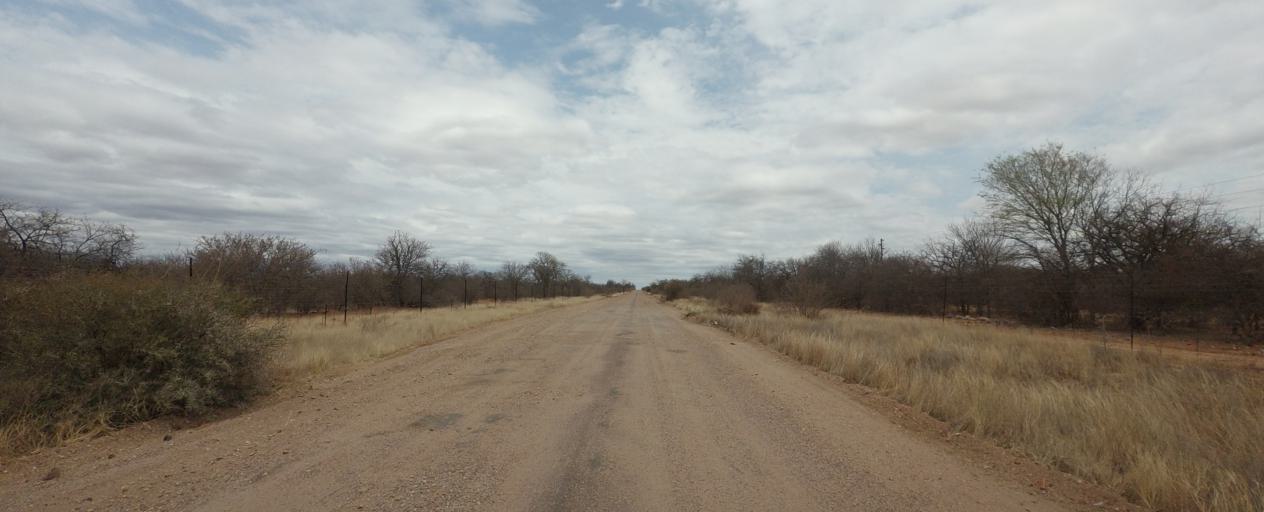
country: BW
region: Central
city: Mathathane
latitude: -22.6685
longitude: 28.6886
